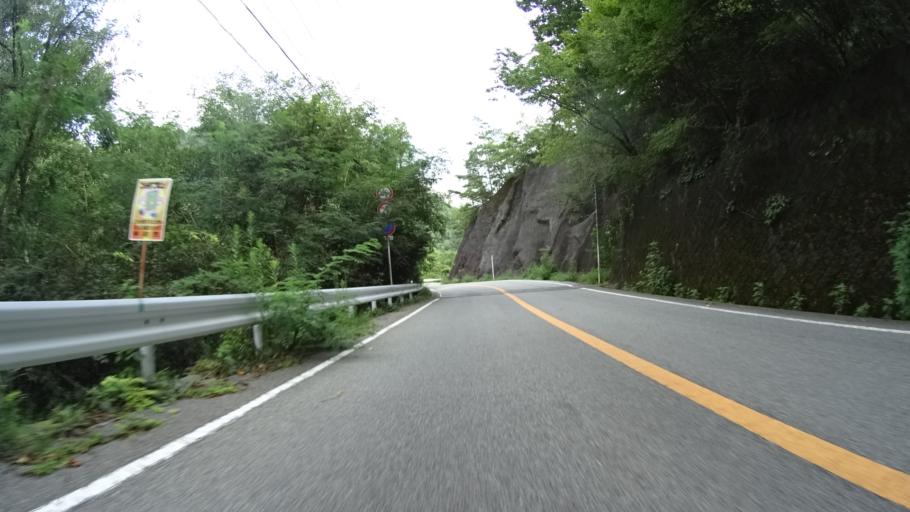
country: JP
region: Yamanashi
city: Kofu-shi
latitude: 35.7005
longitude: 138.5610
